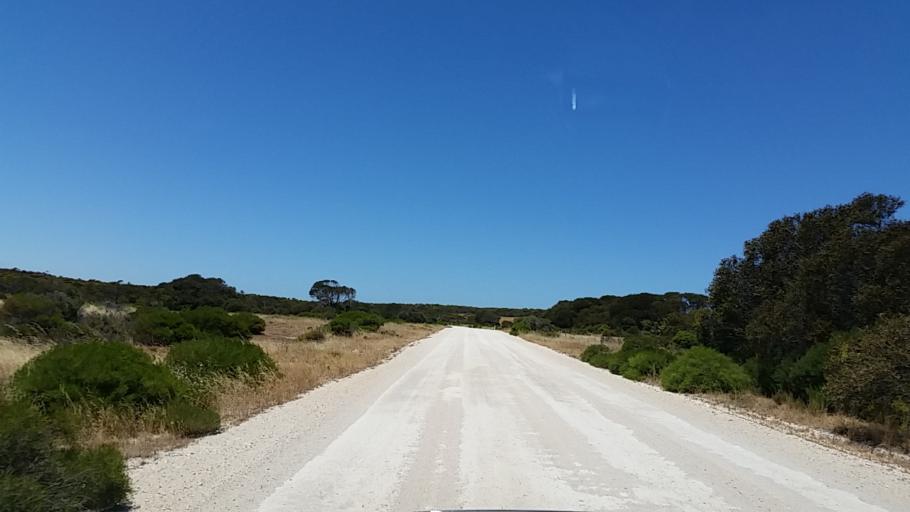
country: AU
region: South Australia
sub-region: Yorke Peninsula
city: Honiton
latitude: -35.2300
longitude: 137.1253
